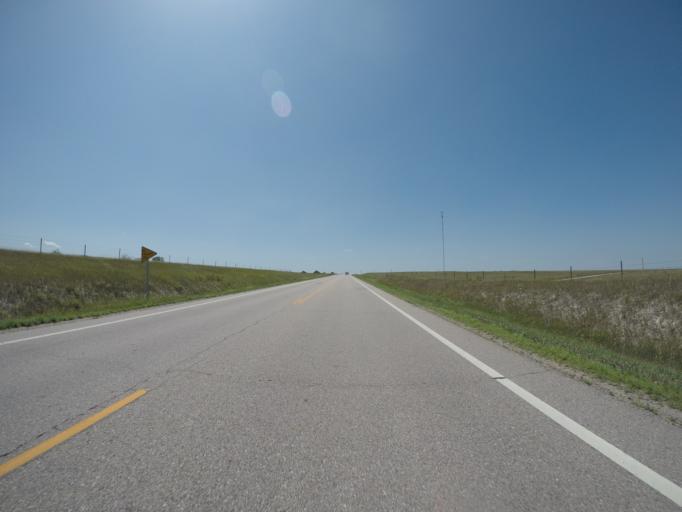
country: US
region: Kansas
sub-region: Osborne County
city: Osborne
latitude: 39.4822
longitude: -98.6953
